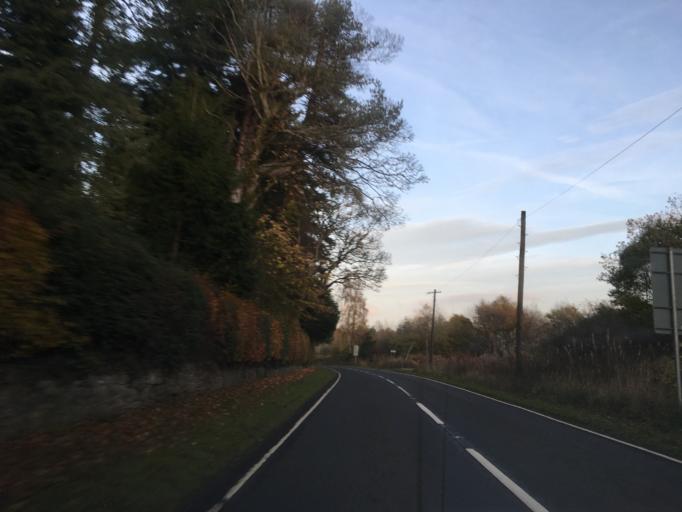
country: GB
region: Scotland
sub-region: Clackmannanshire
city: Dollar
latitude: 56.1640
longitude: -3.6648
